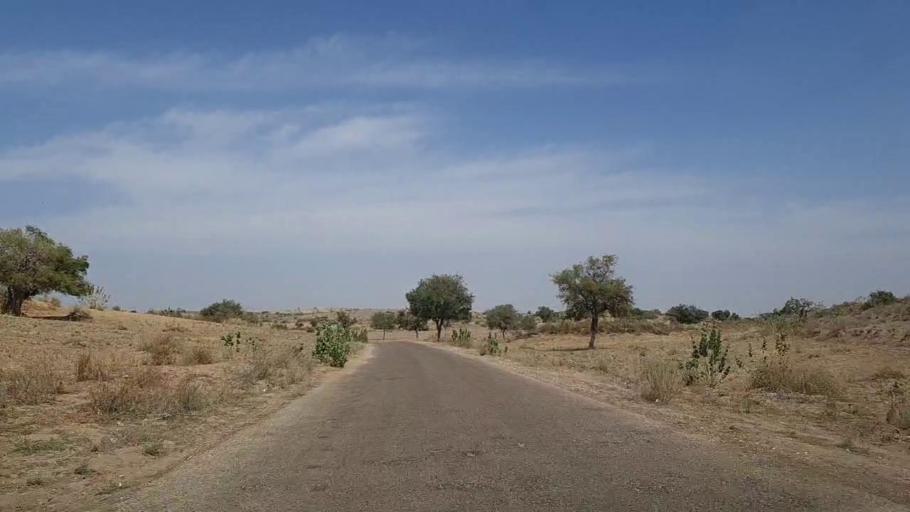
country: PK
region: Sindh
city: Umarkot
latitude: 25.1388
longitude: 70.0115
